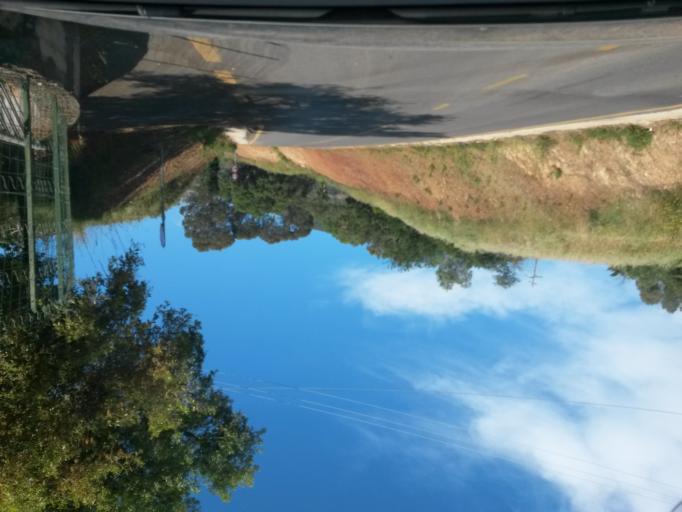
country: IT
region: Tuscany
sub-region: Provincia di Livorno
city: Rio nell'Elba
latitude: 42.8107
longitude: 10.4124
